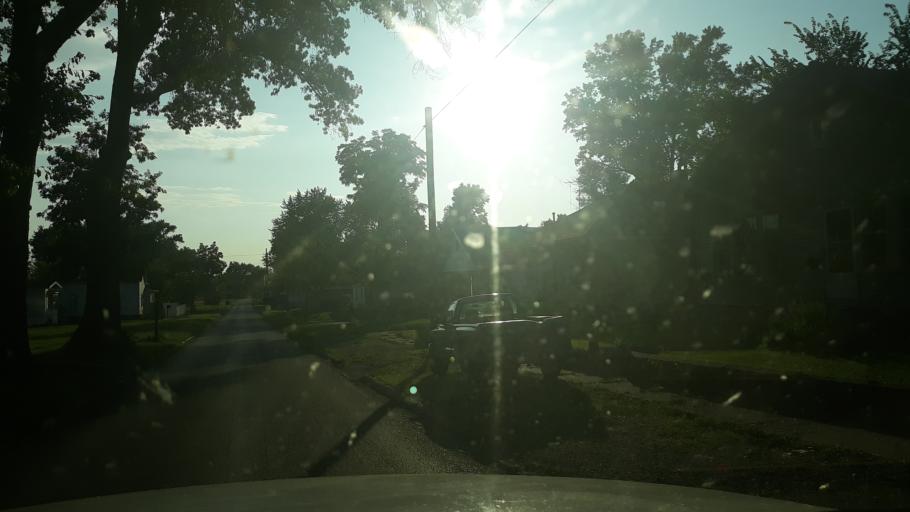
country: US
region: Illinois
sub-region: Saline County
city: Eldorado
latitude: 37.8125
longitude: -88.4321
